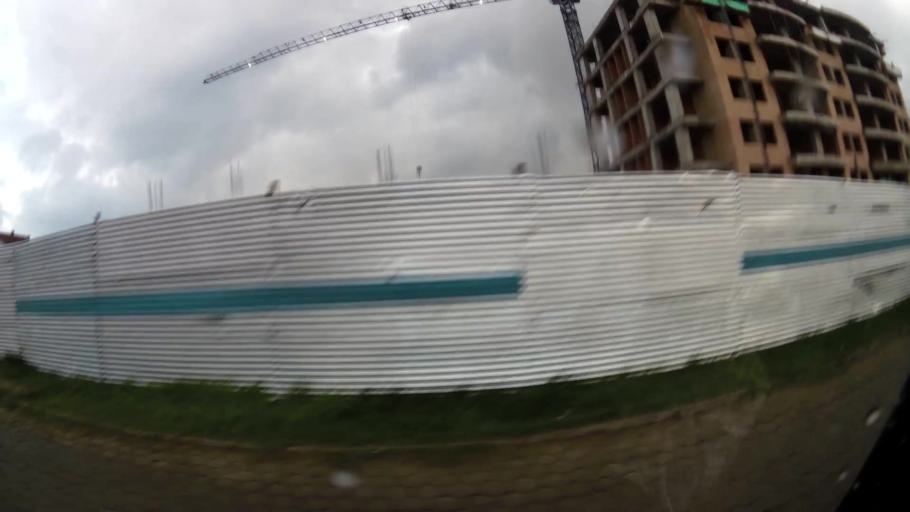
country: CO
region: Cundinamarca
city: Chia
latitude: 4.8672
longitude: -74.0610
